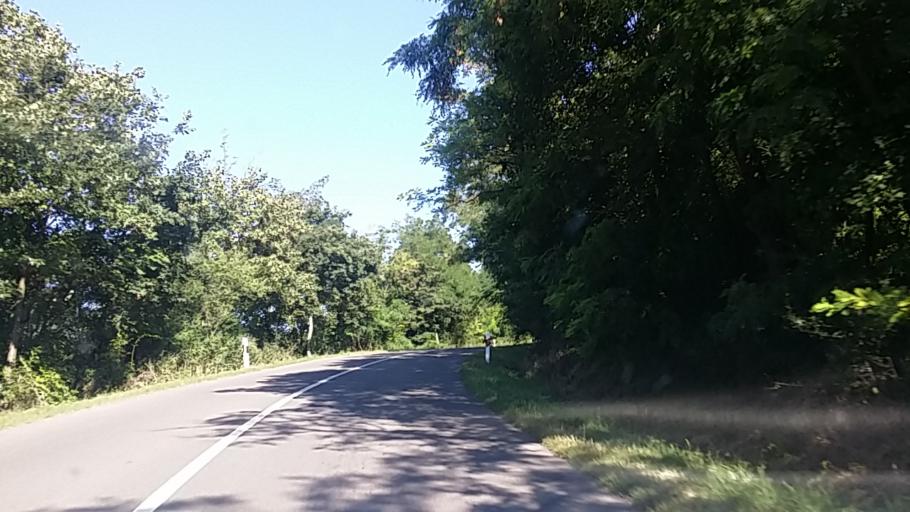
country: HU
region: Nograd
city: Bujak
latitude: 47.9253
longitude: 19.6151
